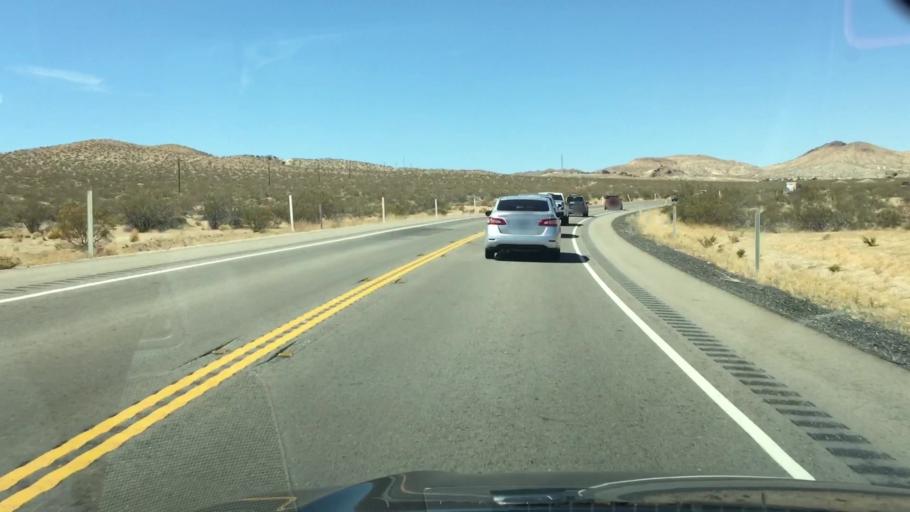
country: US
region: California
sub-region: Kern County
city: Ridgecrest
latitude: 35.3301
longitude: -117.6181
